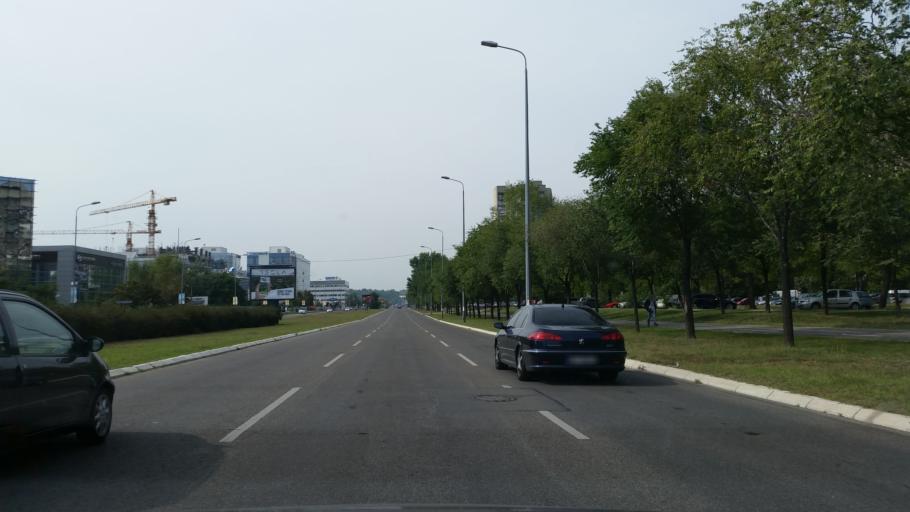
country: RS
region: Central Serbia
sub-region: Belgrade
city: Novi Beograd
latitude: 44.8110
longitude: 20.4139
